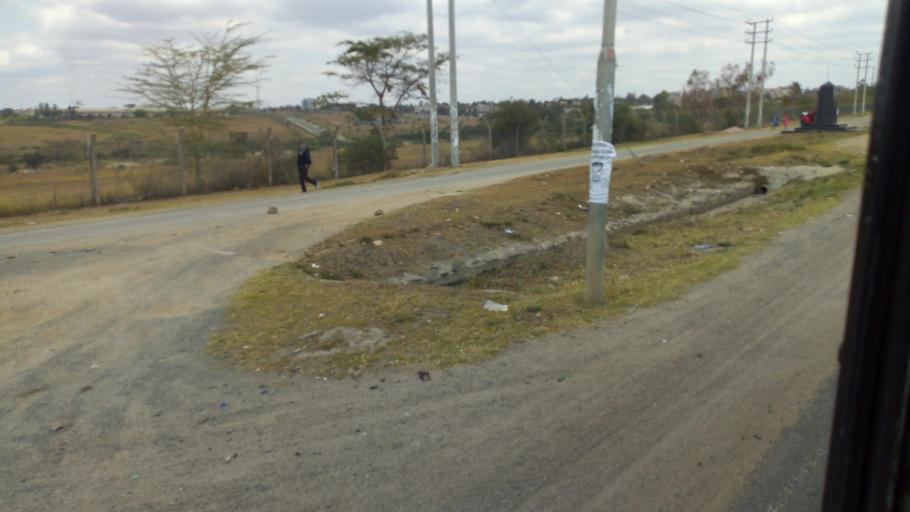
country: KE
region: Machakos
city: Athi River
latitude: -1.4632
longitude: 36.9630
